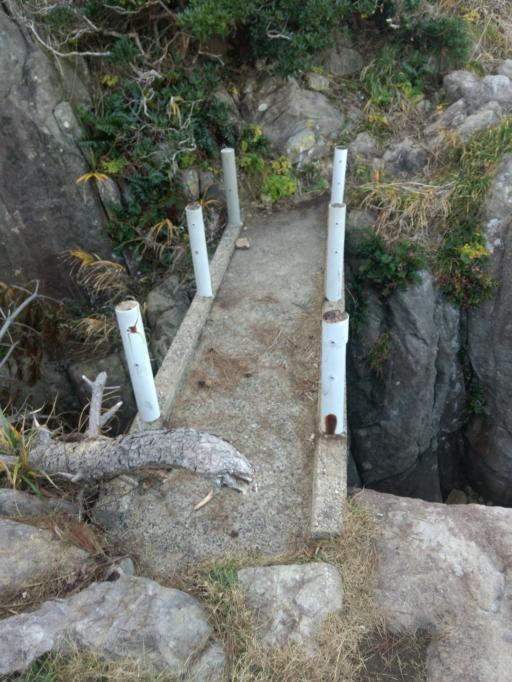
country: JP
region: Kyoto
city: Miyazu
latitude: 35.7785
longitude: 135.2233
